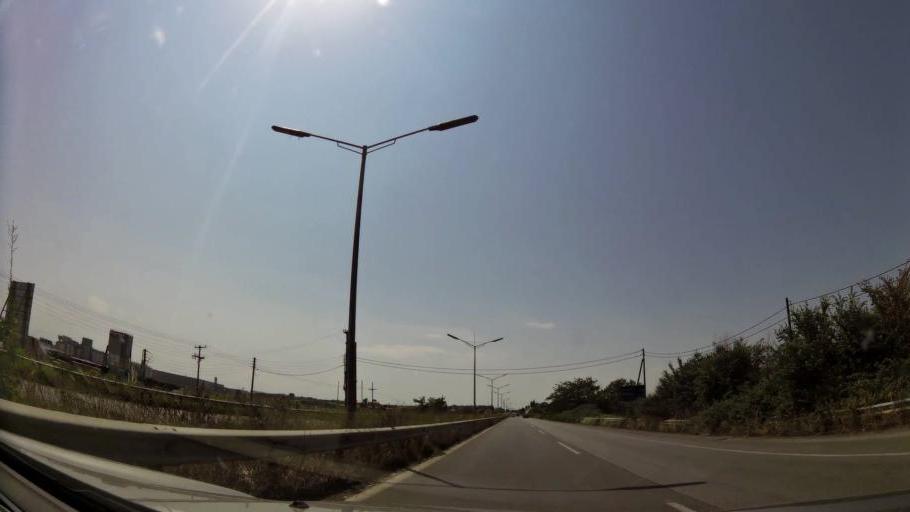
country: GR
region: Central Macedonia
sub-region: Nomos Thessalonikis
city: Agios Athanasios
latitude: 40.7082
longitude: 22.7697
